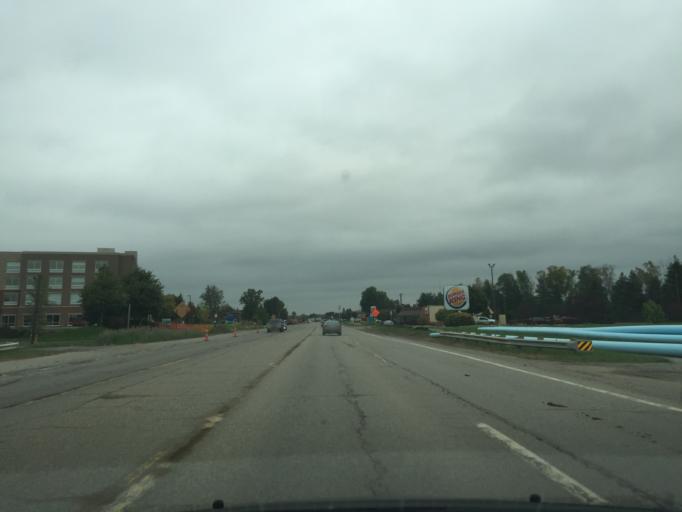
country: US
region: Michigan
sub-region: Oakland County
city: Auburn Hills
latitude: 42.6508
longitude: -83.2475
